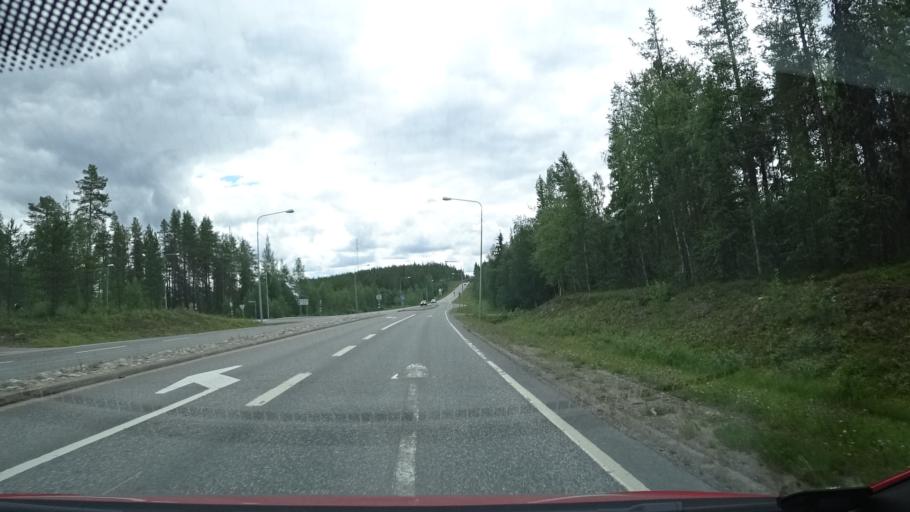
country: FI
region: Lapland
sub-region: Tunturi-Lappi
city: Kittilae
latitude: 67.7682
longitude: 24.8438
